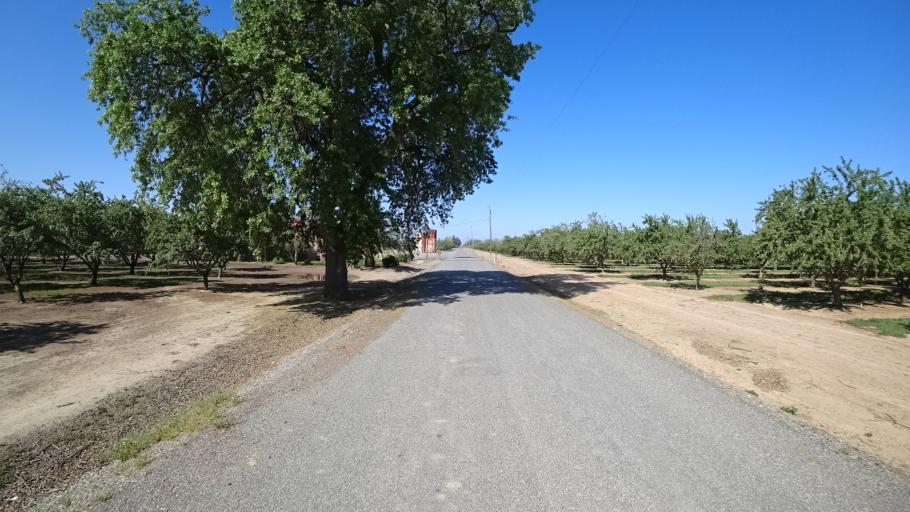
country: US
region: California
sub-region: Glenn County
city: Hamilton City
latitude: 39.6596
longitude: -122.0032
